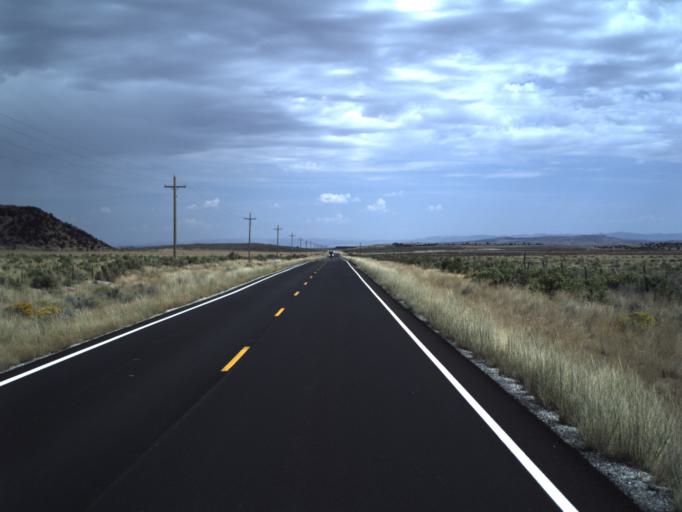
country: US
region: Idaho
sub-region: Minidoka County
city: Heyburn
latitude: 41.8230
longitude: -113.1858
